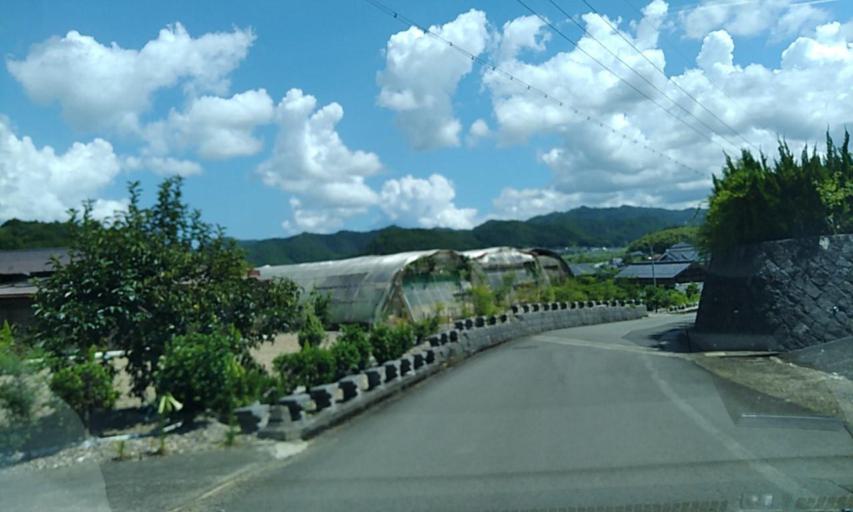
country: JP
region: Kyoto
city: Ayabe
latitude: 35.3537
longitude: 135.2344
